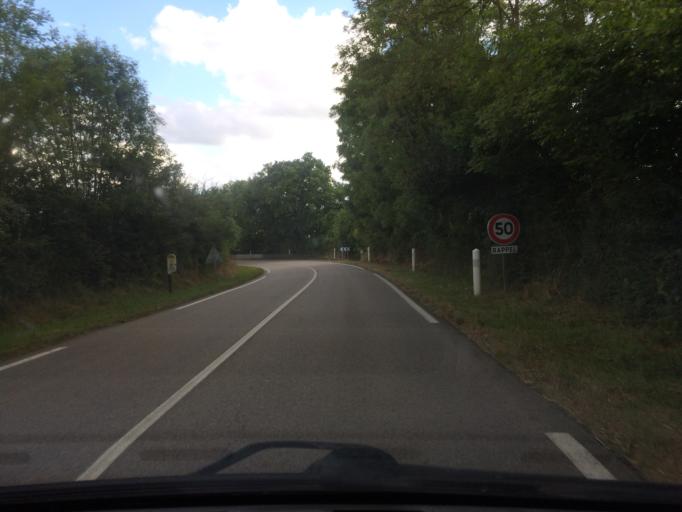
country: FR
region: Lower Normandy
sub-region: Departement du Calvados
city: Clecy
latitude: 48.8789
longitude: -0.4101
